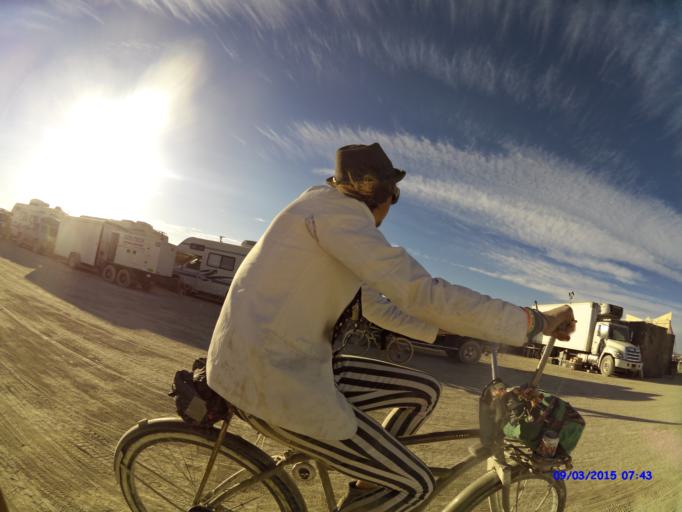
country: US
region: Nevada
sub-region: Pershing County
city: Lovelock
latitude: 40.7926
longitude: -119.2134
